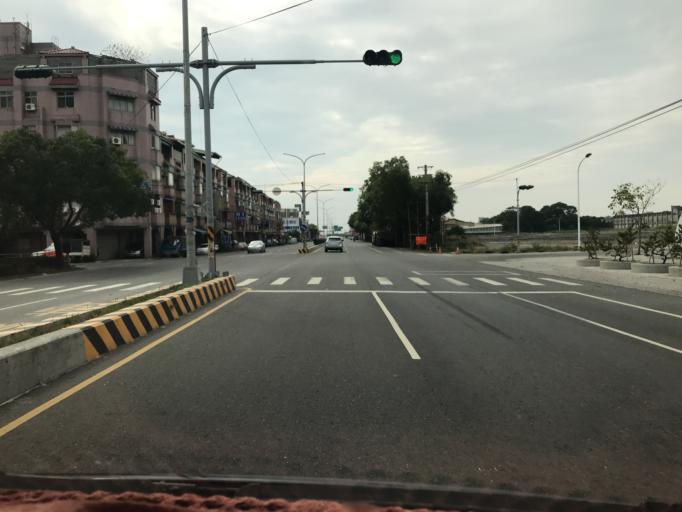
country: TW
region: Taiwan
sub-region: Yunlin
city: Douliu
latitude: 23.7632
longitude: 120.6153
